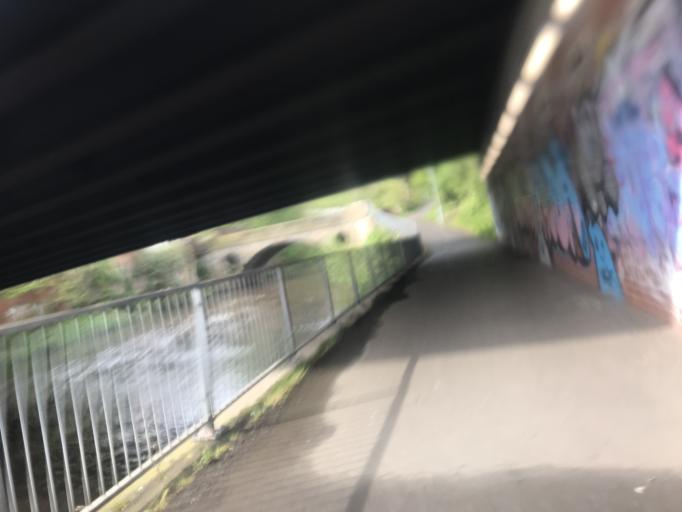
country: GB
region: England
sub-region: Borough of Stockport
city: Stockport
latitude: 53.4078
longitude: -2.1739
